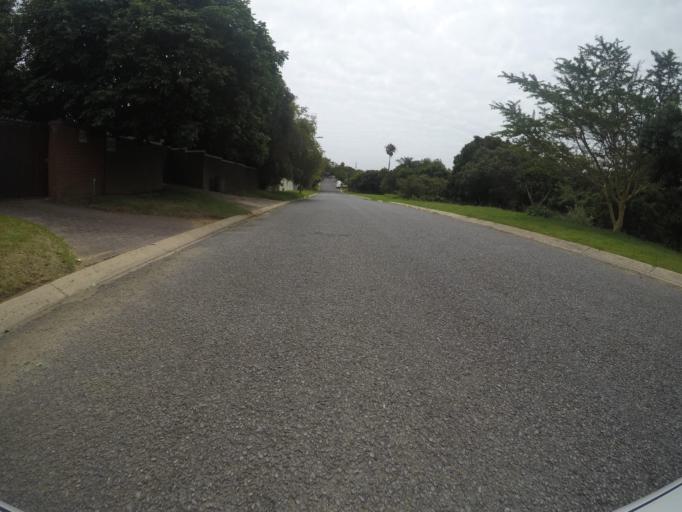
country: ZA
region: Eastern Cape
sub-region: Buffalo City Metropolitan Municipality
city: East London
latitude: -32.9751
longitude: 27.9488
